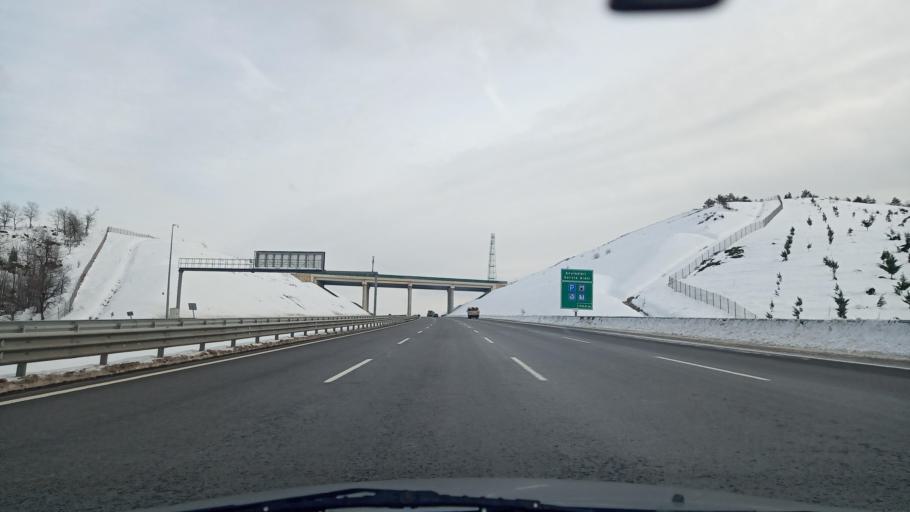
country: TR
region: Kocaeli
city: Hereke
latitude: 40.8912
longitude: 29.6853
